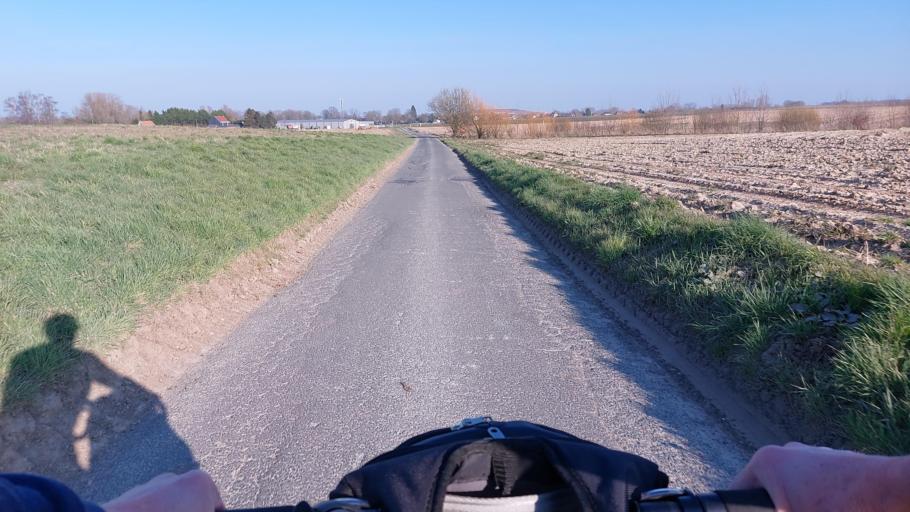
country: BE
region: Wallonia
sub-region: Province du Hainaut
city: Jurbise
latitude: 50.5635
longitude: 3.9866
